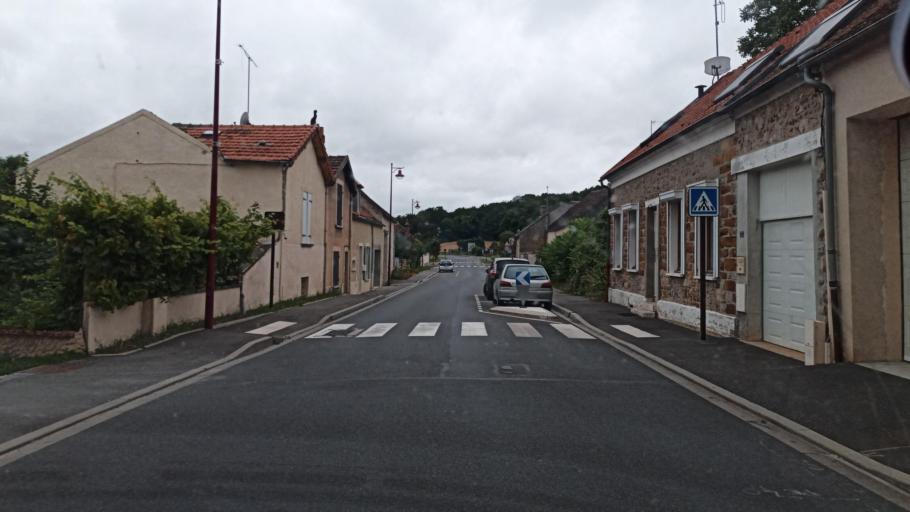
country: FR
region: Ile-de-France
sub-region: Departement de Seine-et-Marne
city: Voulx
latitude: 48.2870
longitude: 2.9591
